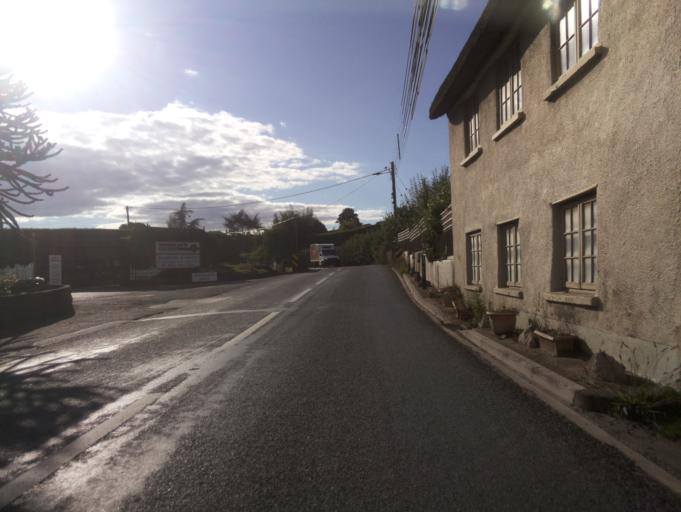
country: GB
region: England
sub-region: Devon
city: Newton Poppleford
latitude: 50.6985
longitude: -3.3103
